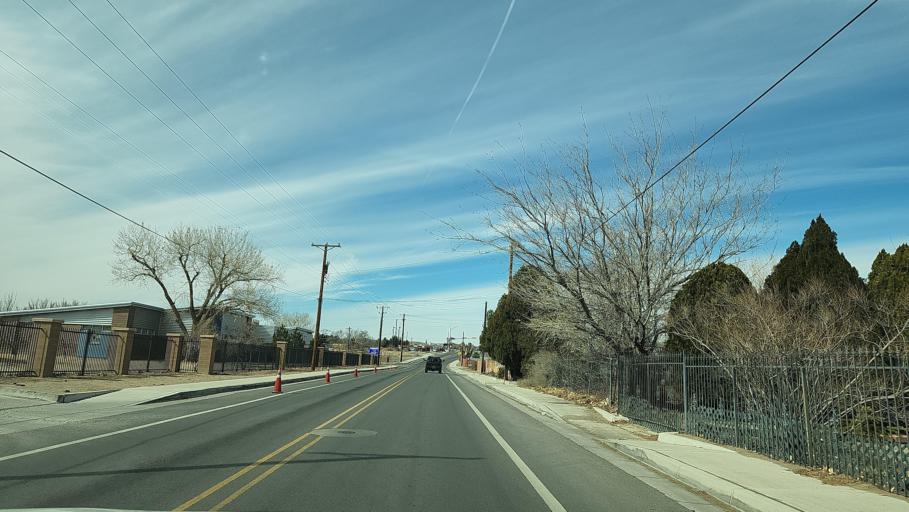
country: US
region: New Mexico
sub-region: Bernalillo County
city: South Valley
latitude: 35.0362
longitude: -106.7089
